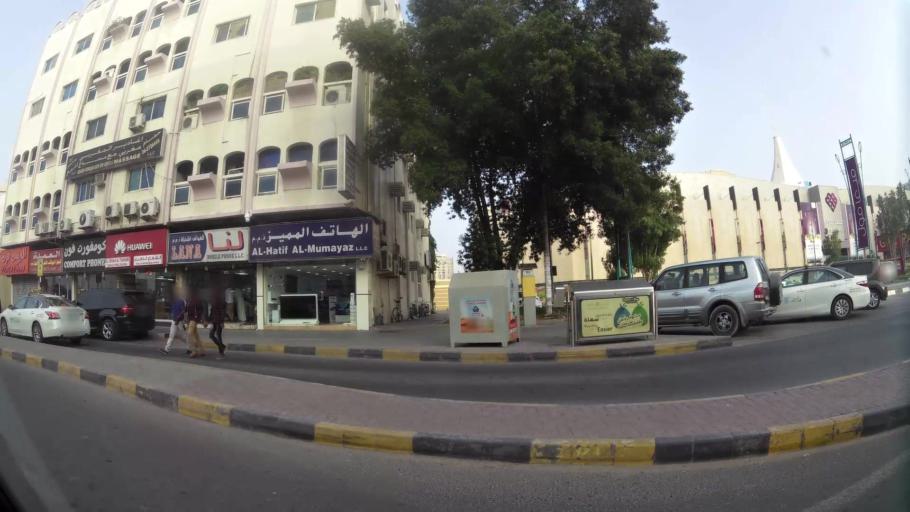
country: AE
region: Ash Shariqah
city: Sharjah
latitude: 25.3463
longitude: 55.3982
